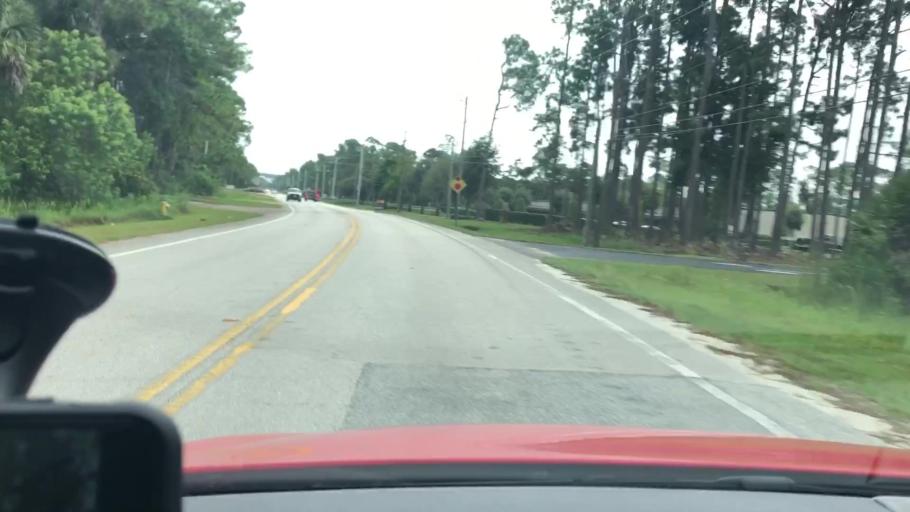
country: US
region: Florida
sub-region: Volusia County
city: Holly Hill
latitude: 29.2050
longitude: -81.0847
